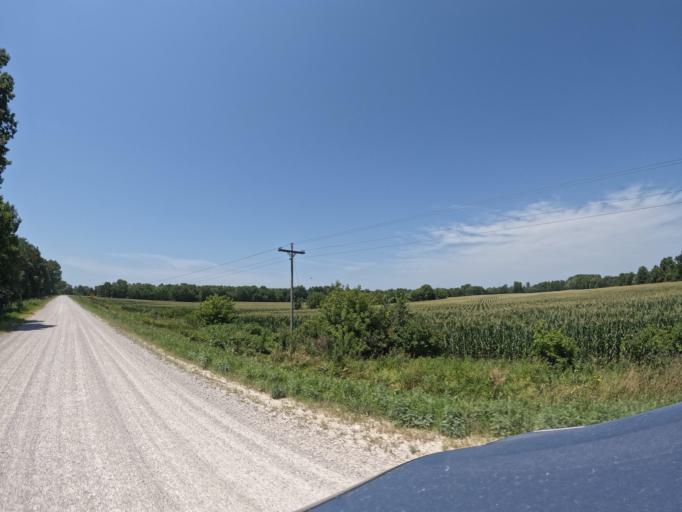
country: US
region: Iowa
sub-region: Henry County
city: Mount Pleasant
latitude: 40.9654
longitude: -91.6739
